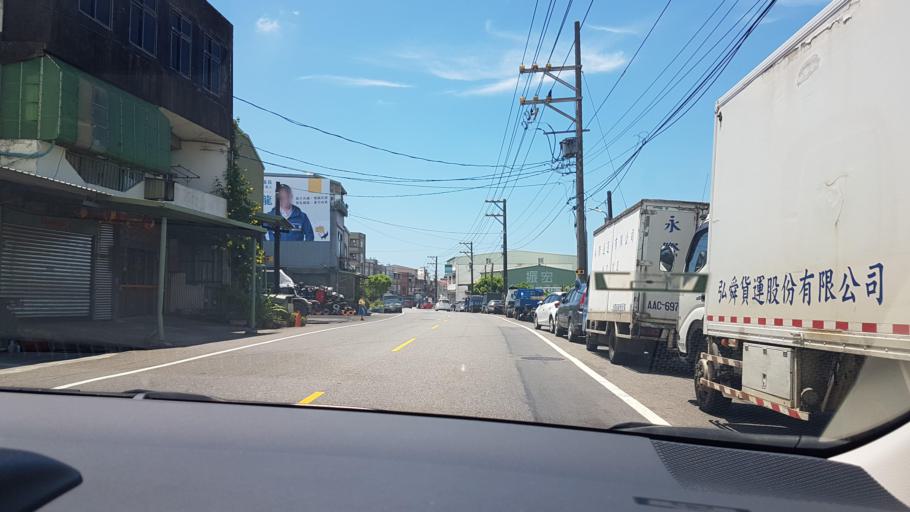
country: TW
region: Taiwan
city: Taoyuan City
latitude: 25.0865
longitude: 121.2839
